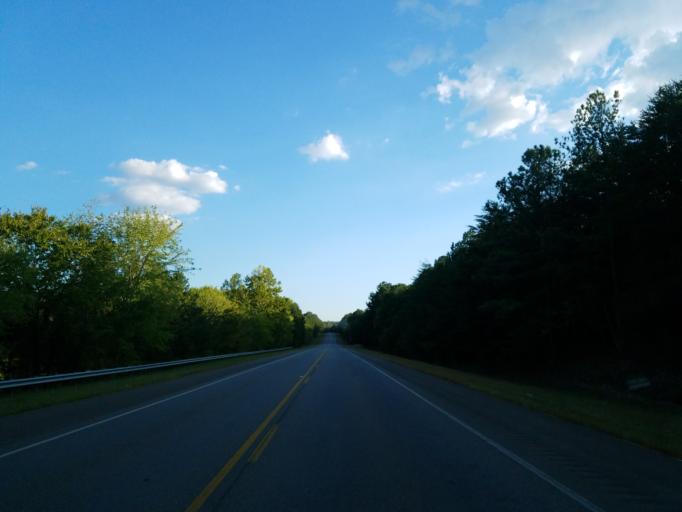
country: US
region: Georgia
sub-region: Murray County
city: Chatsworth
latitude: 34.6112
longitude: -84.7134
